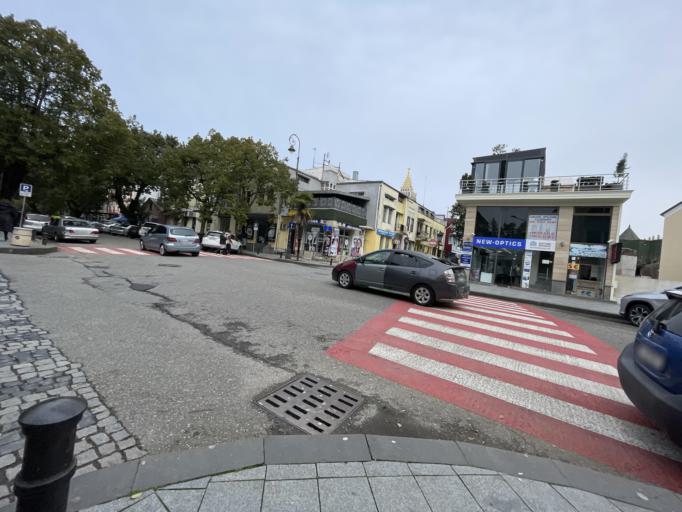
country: GE
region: Ajaria
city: Batumi
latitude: 41.6485
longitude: 41.6397
